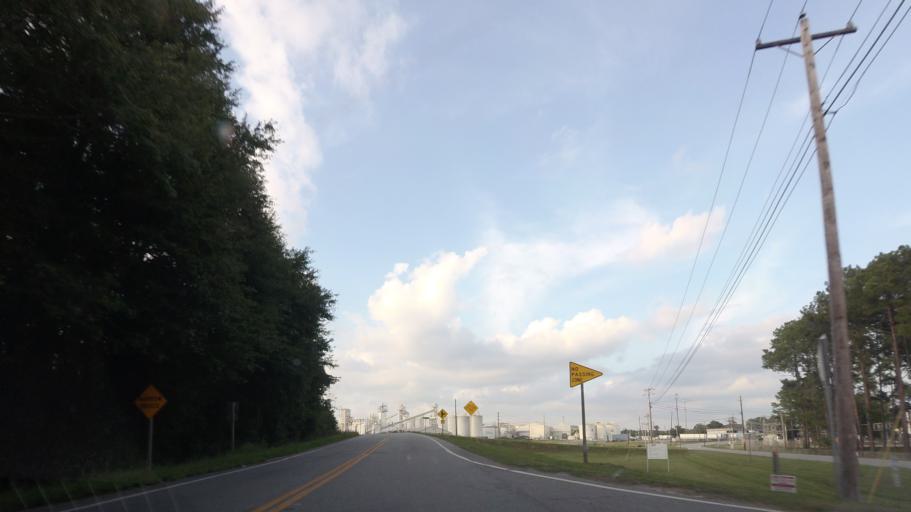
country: US
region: Georgia
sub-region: Wilkinson County
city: Gordon
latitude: 32.8768
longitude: -83.3399
